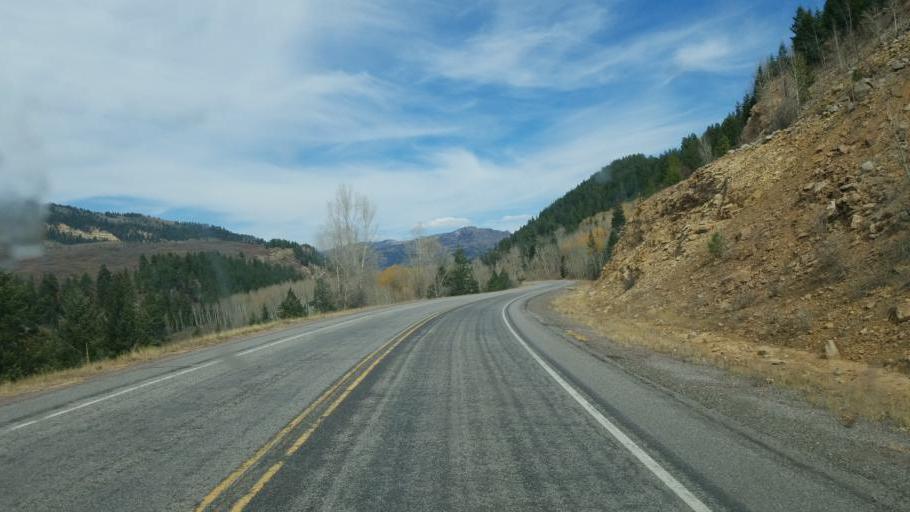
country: US
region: New Mexico
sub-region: Rio Arriba County
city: Chama
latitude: 36.9328
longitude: -106.5537
